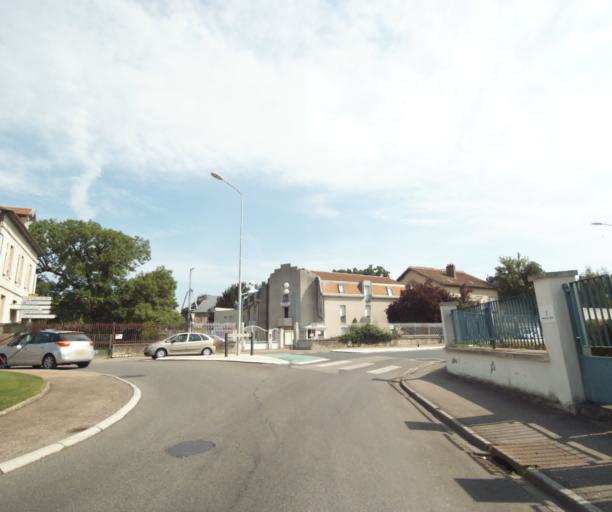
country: FR
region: Lorraine
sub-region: Departement de Meurthe-et-Moselle
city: Luneville
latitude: 48.5910
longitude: 6.5038
